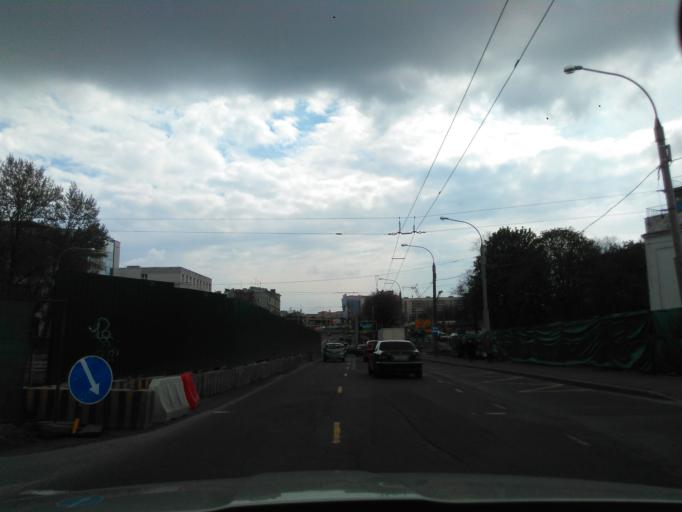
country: BY
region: Minsk
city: Minsk
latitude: 53.8958
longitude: 27.5384
